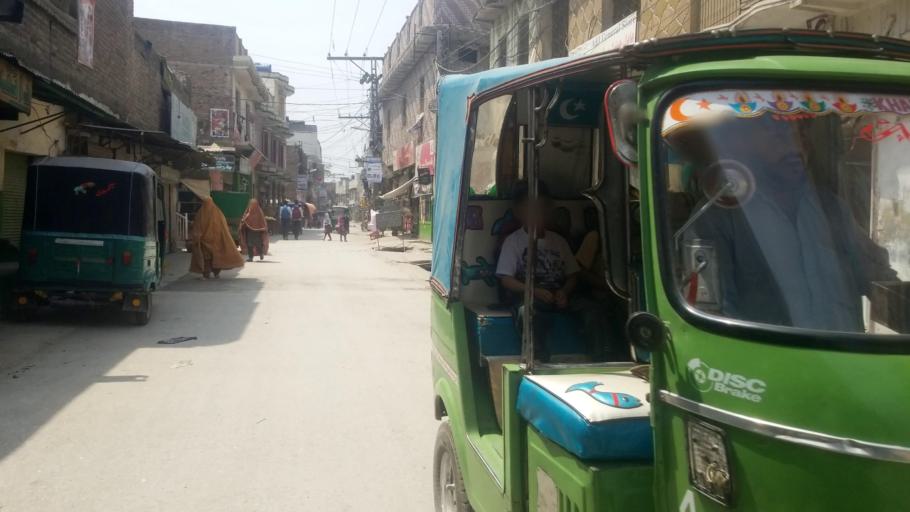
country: PK
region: Khyber Pakhtunkhwa
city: Peshawar
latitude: 34.0293
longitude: 71.5842
